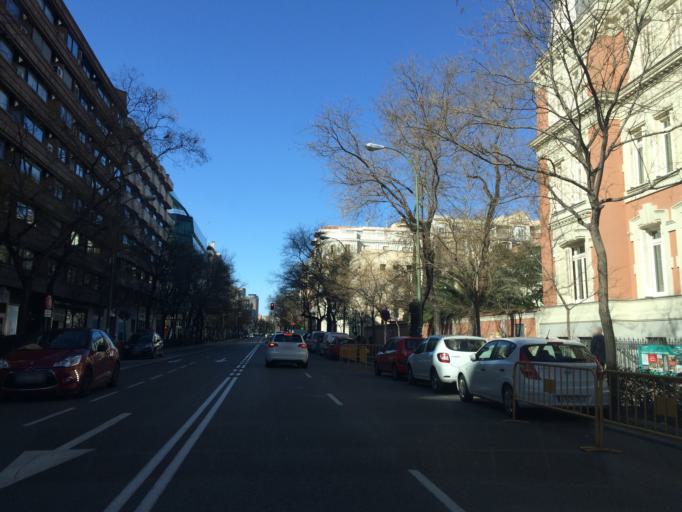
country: ES
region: Madrid
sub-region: Provincia de Madrid
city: Salamanca
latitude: 40.4340
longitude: -3.6913
